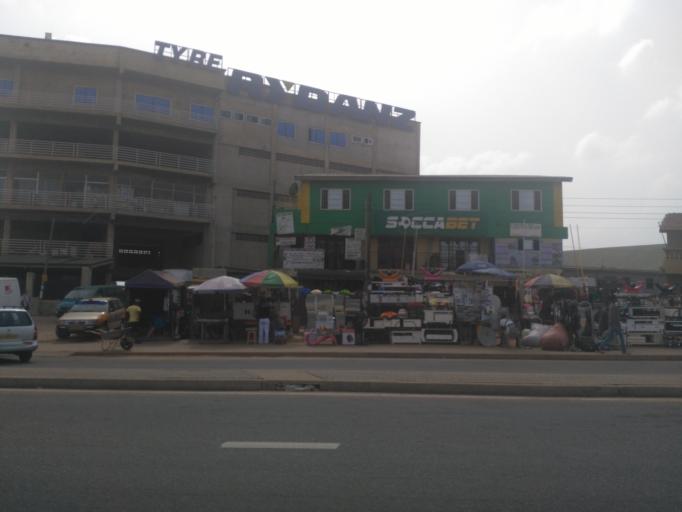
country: GH
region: Greater Accra
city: Dome
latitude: 5.6061
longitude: -0.2501
